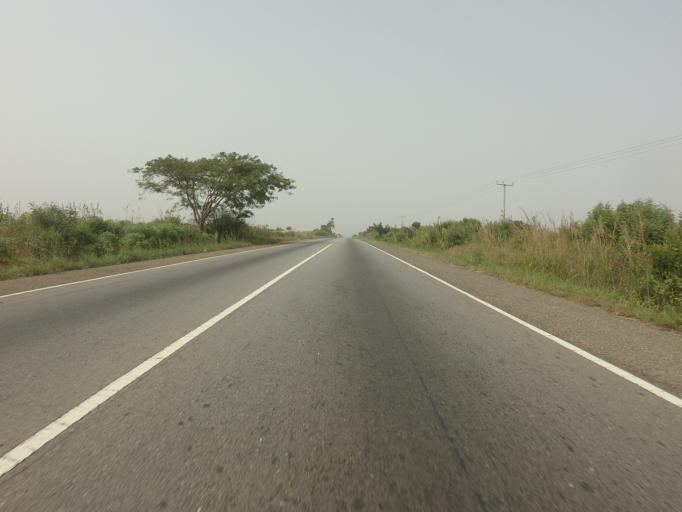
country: GH
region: Volta
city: Anloga
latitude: 5.9421
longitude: 0.5237
